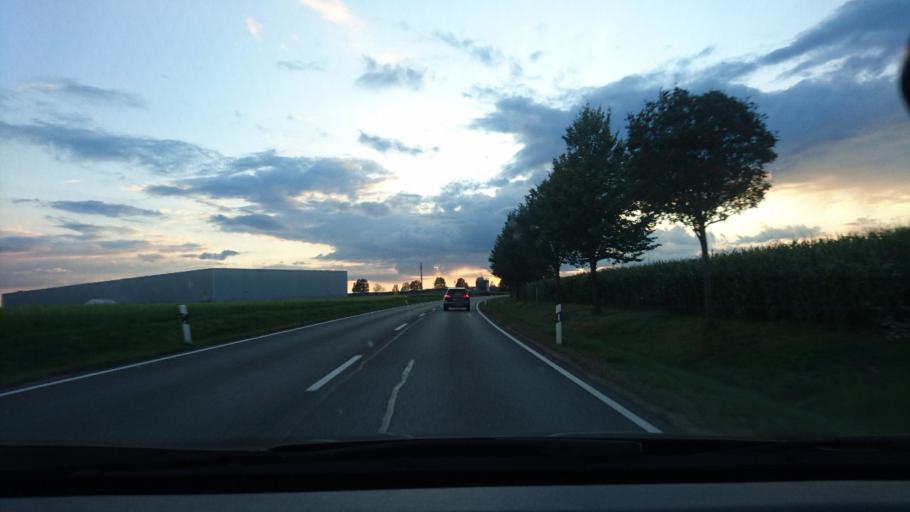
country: DE
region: Saxony
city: Treuen
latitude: 50.5510
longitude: 12.2925
